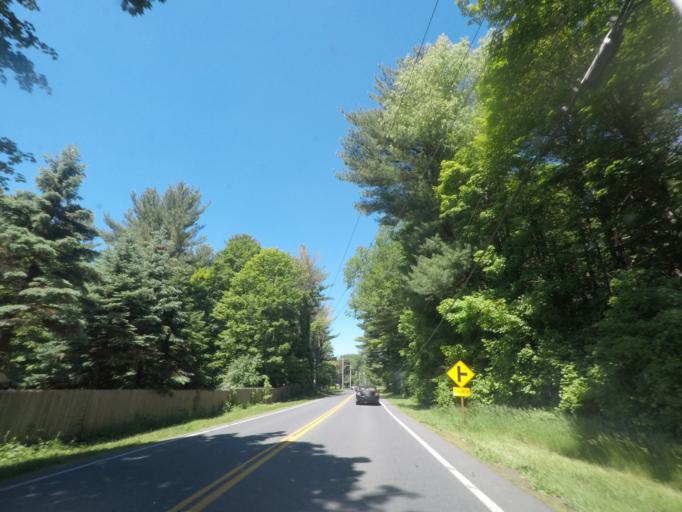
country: US
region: New York
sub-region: Saratoga County
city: Country Knolls
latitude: 42.8566
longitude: -73.8020
